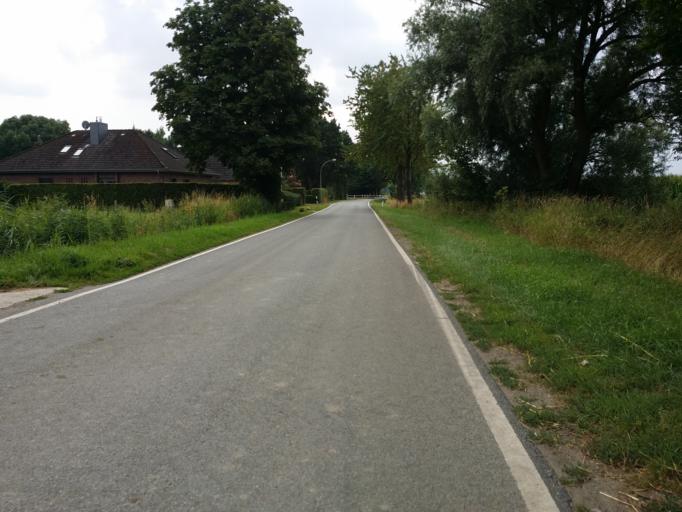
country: DE
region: Schleswig-Holstein
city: Heiligenstedtenerkamp
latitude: 53.8862
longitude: 9.4558
